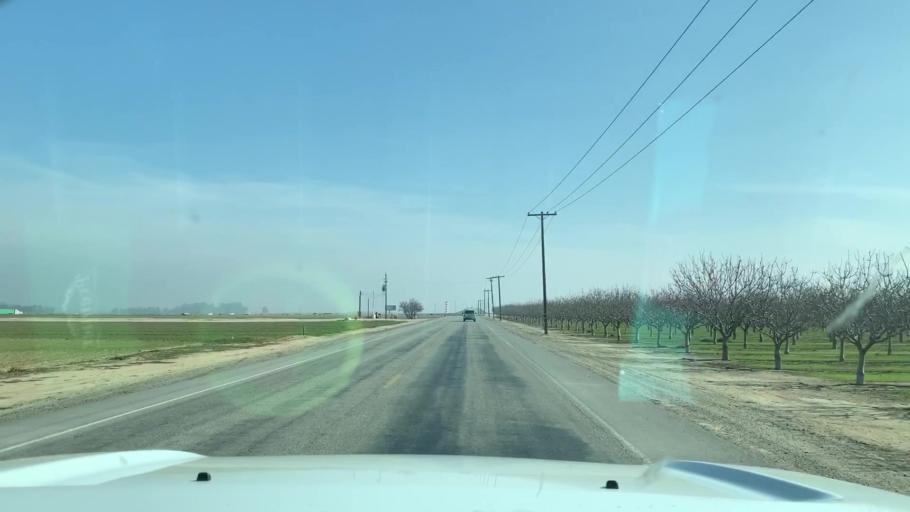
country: US
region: California
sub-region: Kern County
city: Buttonwillow
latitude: 35.4424
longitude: -119.4682
